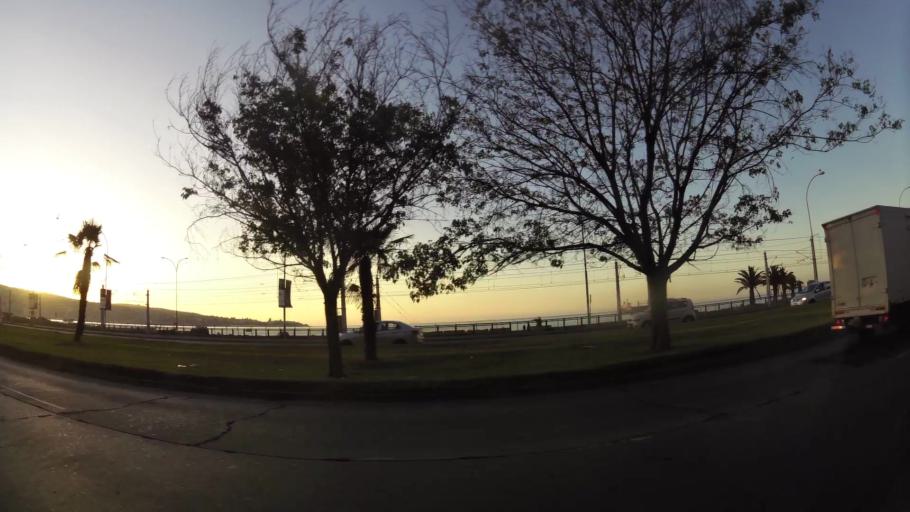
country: CL
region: Valparaiso
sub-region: Provincia de Valparaiso
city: Vina del Mar
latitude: -33.0297
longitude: -71.5867
